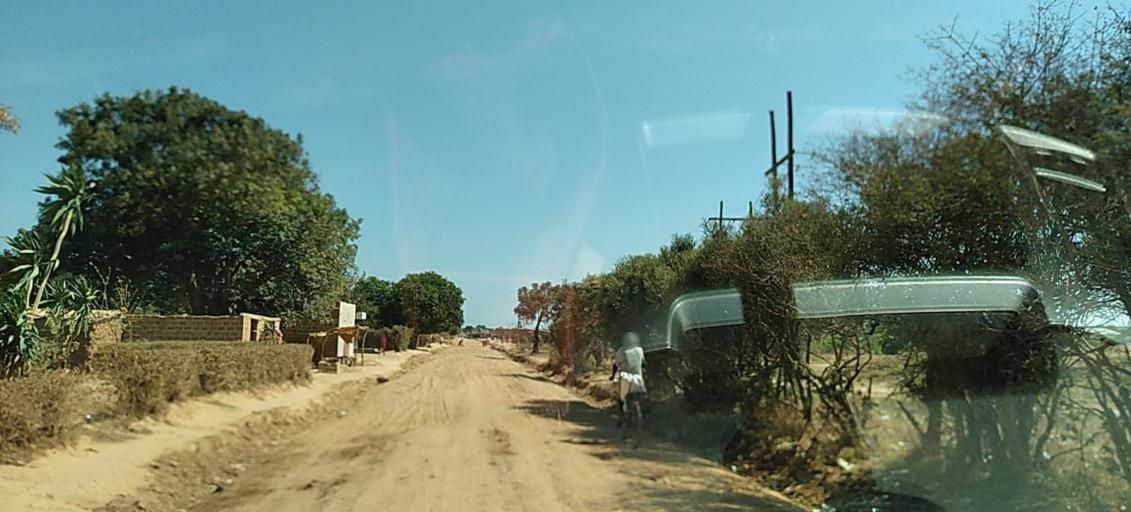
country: ZM
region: Copperbelt
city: Chililabombwe
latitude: -12.3307
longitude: 27.8602
